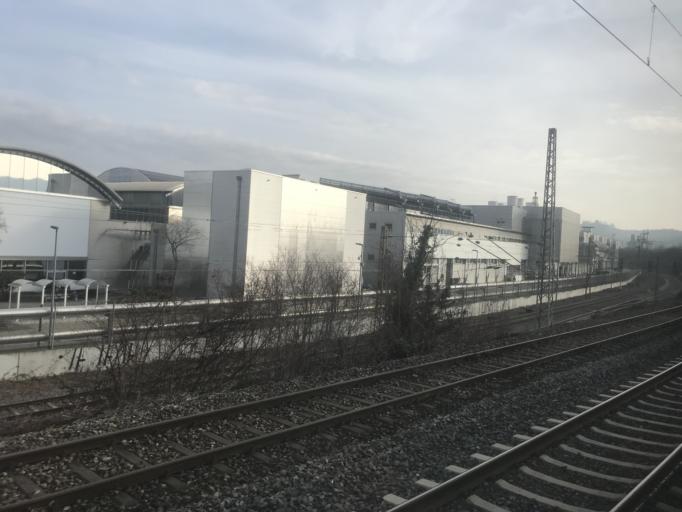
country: DE
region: Baden-Wuerttemberg
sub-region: Regierungsbezirk Stuttgart
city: Stuttgart-Ost
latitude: 48.7972
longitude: 9.2297
